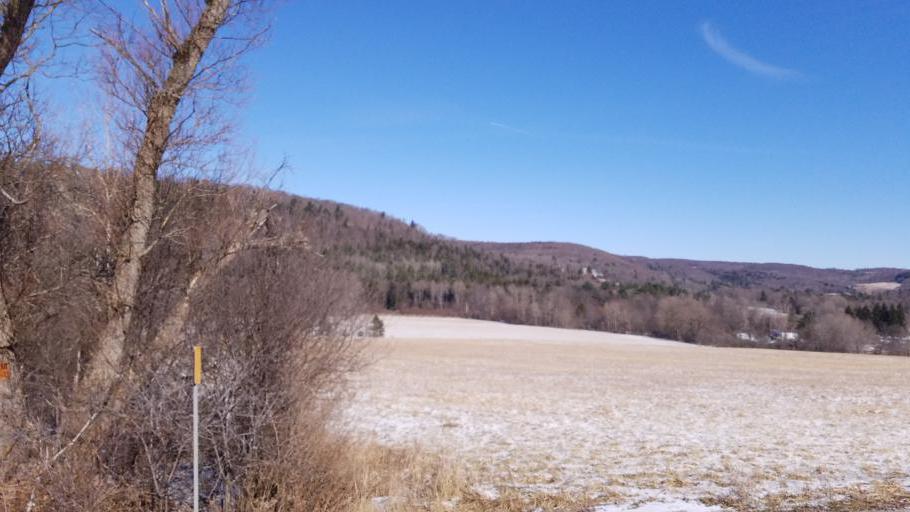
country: US
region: New York
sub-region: Allegany County
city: Wellsville
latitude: 42.0770
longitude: -77.8702
